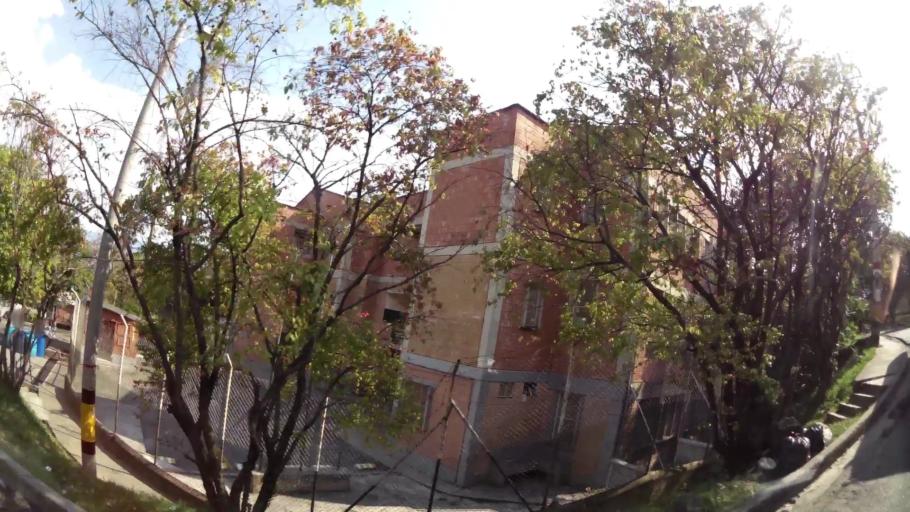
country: CO
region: Antioquia
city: Medellin
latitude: 6.2929
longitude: -75.5937
